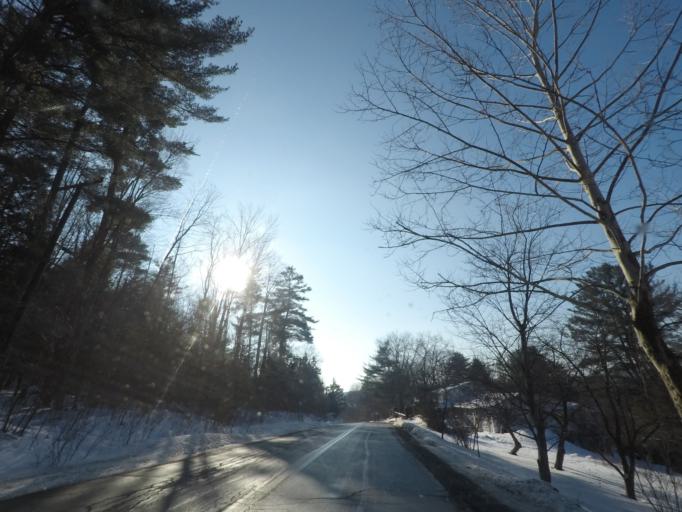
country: US
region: Massachusetts
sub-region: Berkshire County
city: Richmond
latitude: 42.5319
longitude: -73.4051
